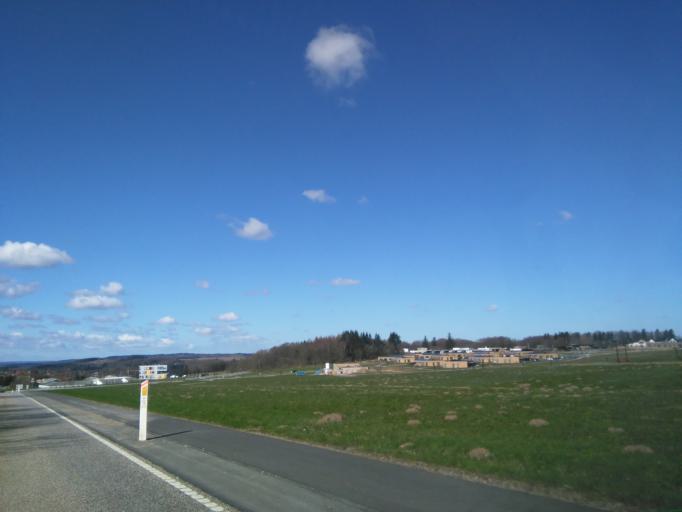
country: DK
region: Central Jutland
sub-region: Skanderborg Kommune
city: Ry
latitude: 56.0881
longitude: 9.7911
